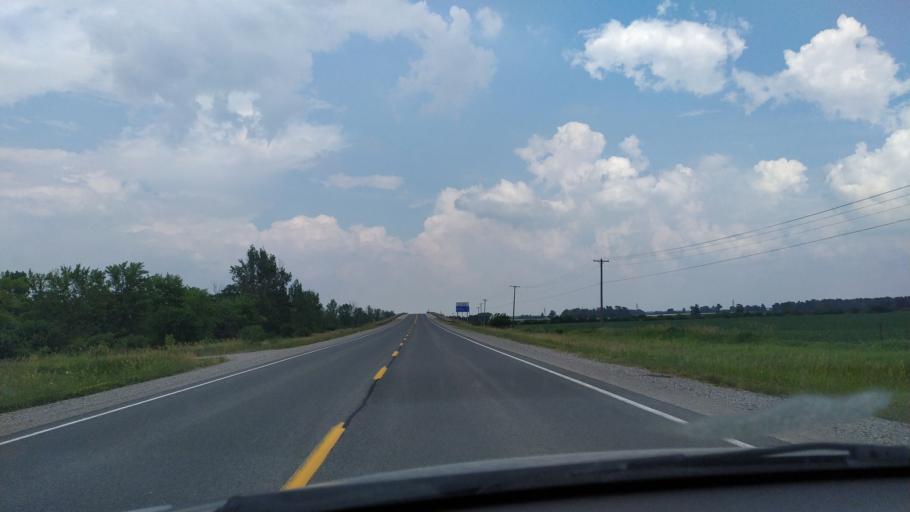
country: CA
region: Ontario
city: Stratford
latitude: 43.2285
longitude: -81.1421
